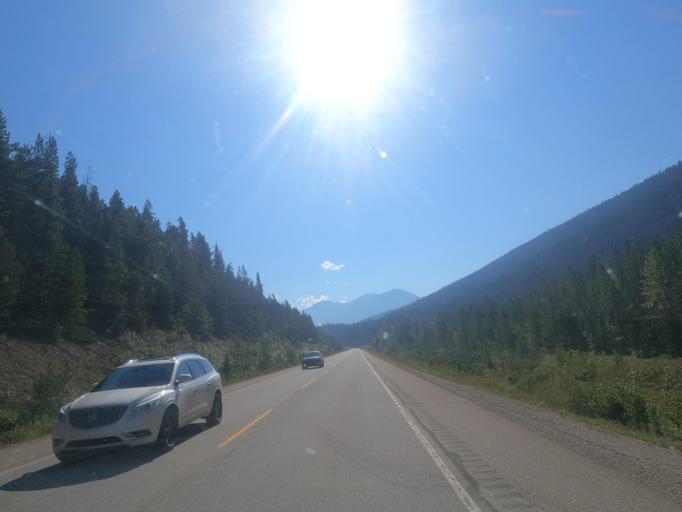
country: CA
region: Alberta
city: Jasper Park Lodge
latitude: 52.8693
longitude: -118.6778
